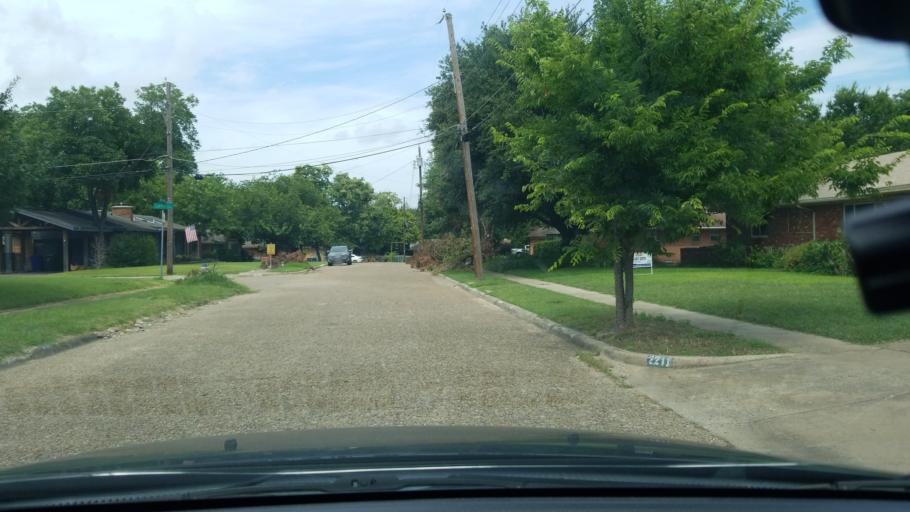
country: US
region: Texas
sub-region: Dallas County
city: Garland
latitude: 32.8249
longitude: -96.6785
